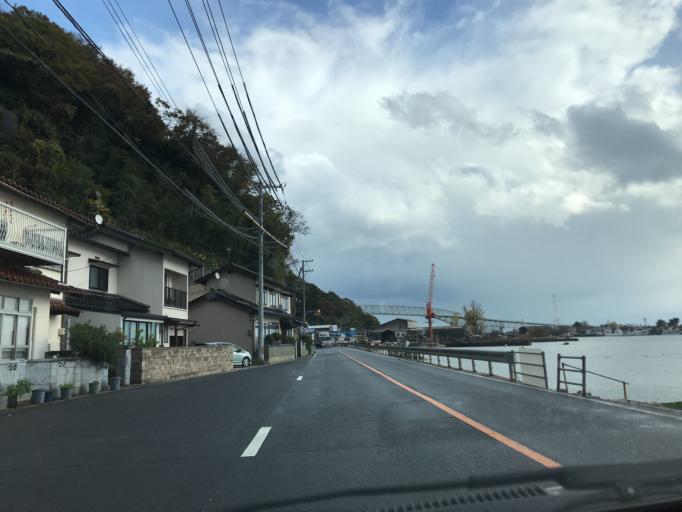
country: JP
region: Shimane
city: Sakaiminato
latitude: 35.5513
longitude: 133.2347
